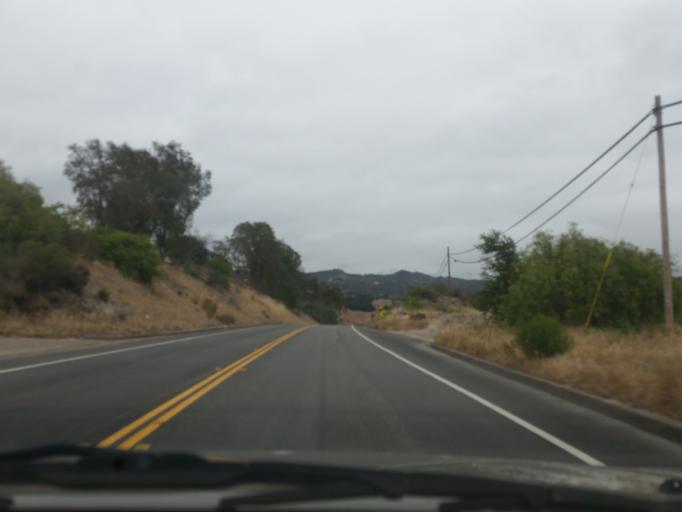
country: US
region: California
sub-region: San Luis Obispo County
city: Avila Beach
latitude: 35.1959
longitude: -120.7046
